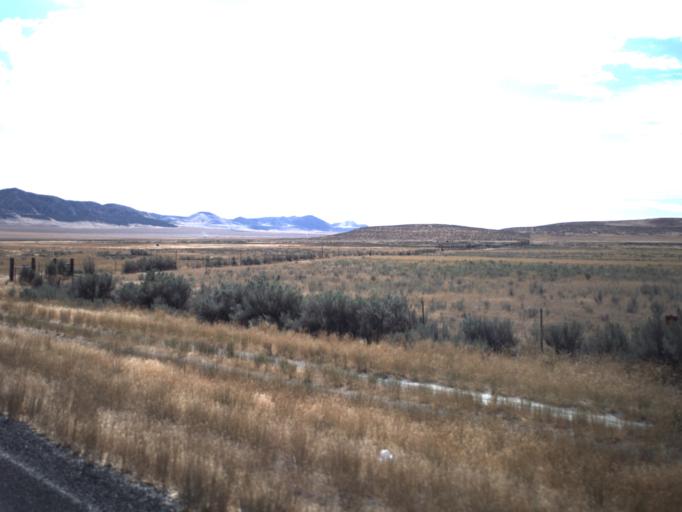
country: US
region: Idaho
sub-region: Oneida County
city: Malad City
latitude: 41.9648
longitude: -112.7659
